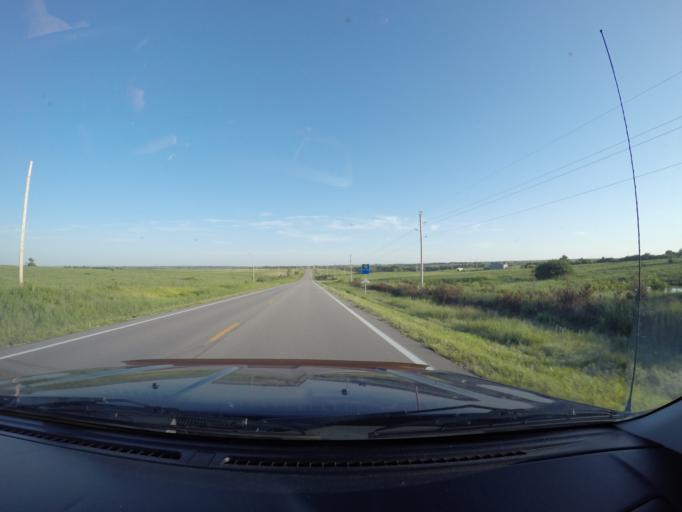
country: US
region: Kansas
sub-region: Wabaunsee County
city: Alma
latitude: 39.0936
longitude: -96.2891
